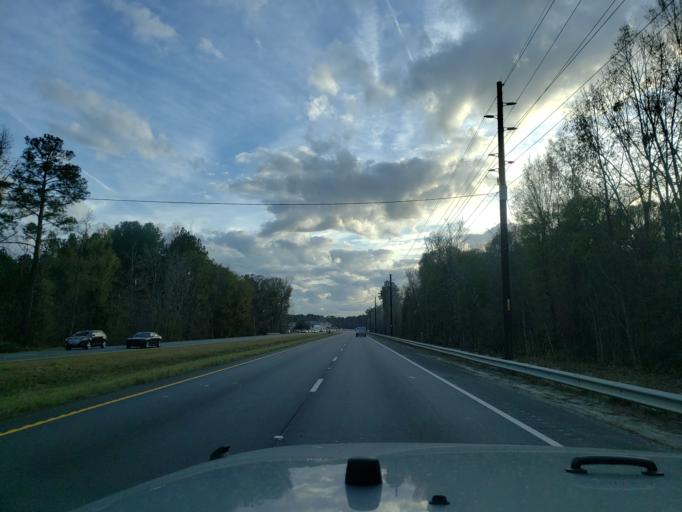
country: US
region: Georgia
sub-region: Chatham County
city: Port Wentworth
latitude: 32.2195
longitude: -81.1971
